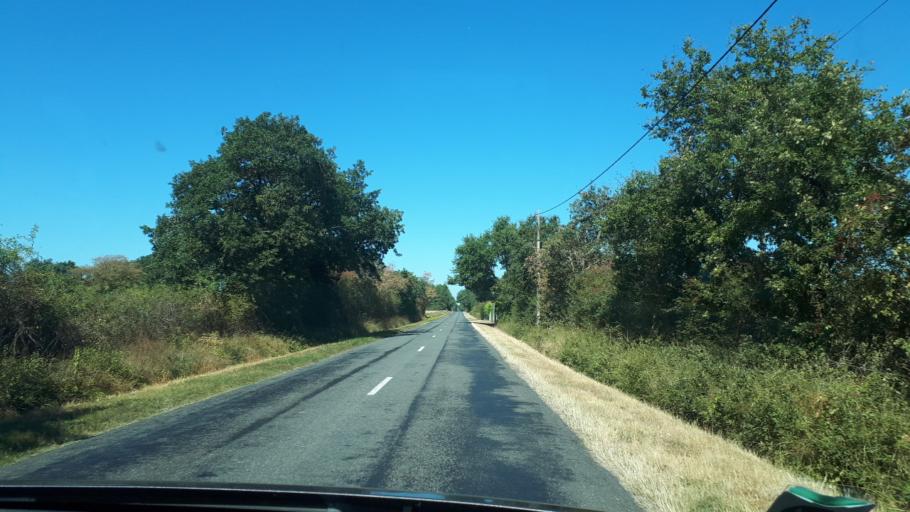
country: FR
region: Centre
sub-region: Departement du Loiret
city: Coullons
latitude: 47.6313
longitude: 2.4679
